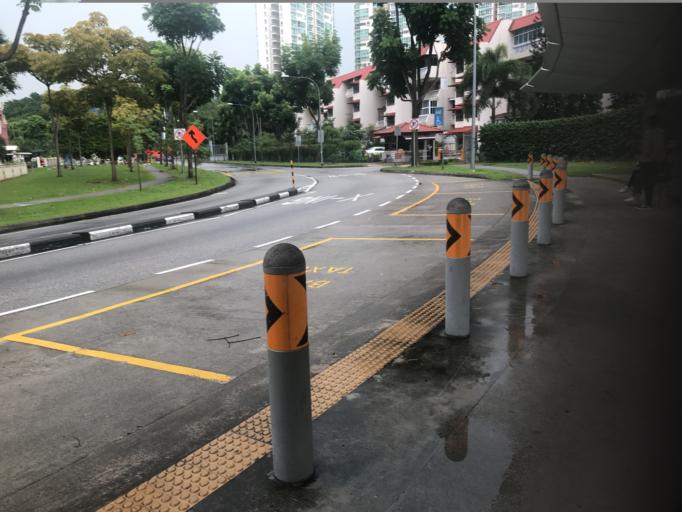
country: SG
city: Singapore
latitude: 1.3516
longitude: 103.8643
